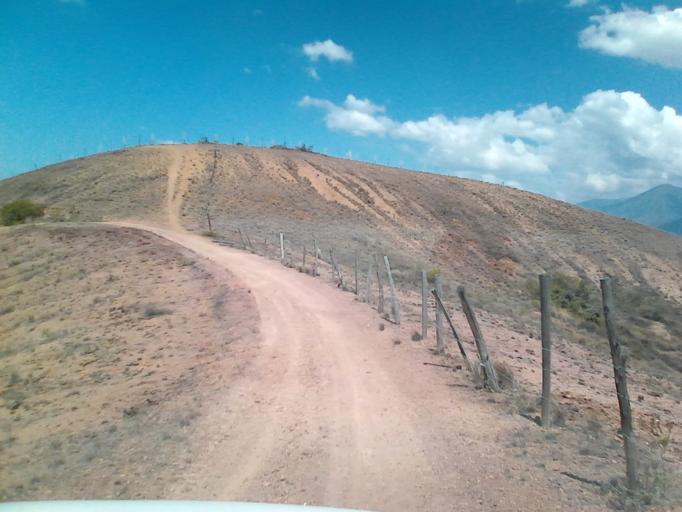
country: CO
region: Boyaca
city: Villa de Leiva
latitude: 5.6098
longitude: -73.5728
